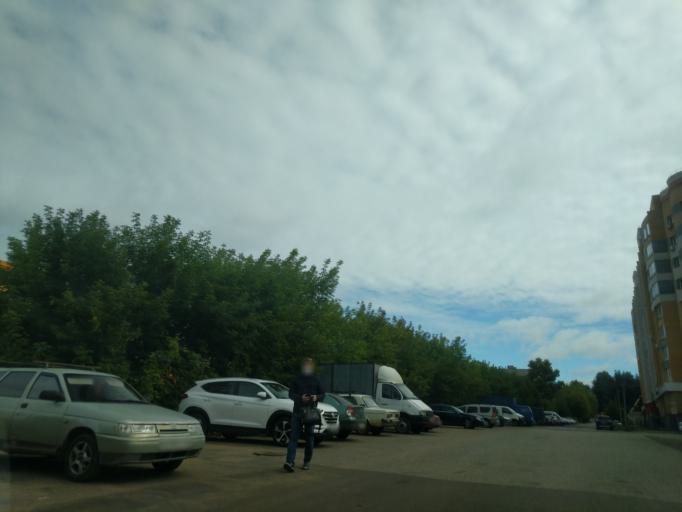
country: RU
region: Kirov
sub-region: Kirovo-Chepetskiy Rayon
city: Kirov
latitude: 58.5977
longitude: 49.6457
